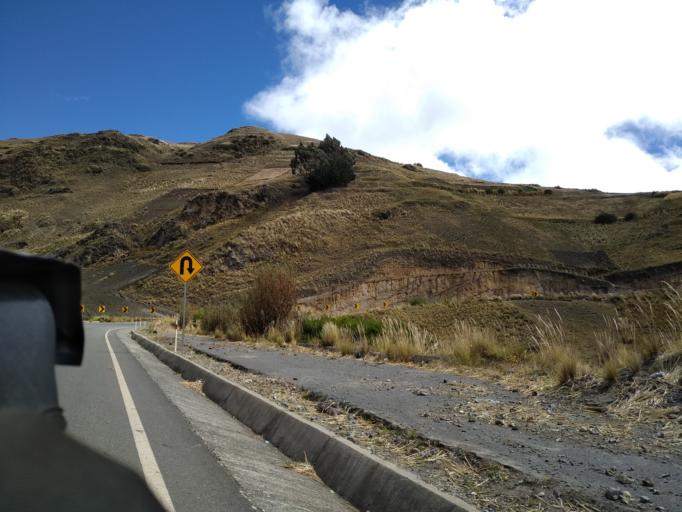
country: EC
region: Cotopaxi
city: Pujili
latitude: -0.9571
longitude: -78.9118
